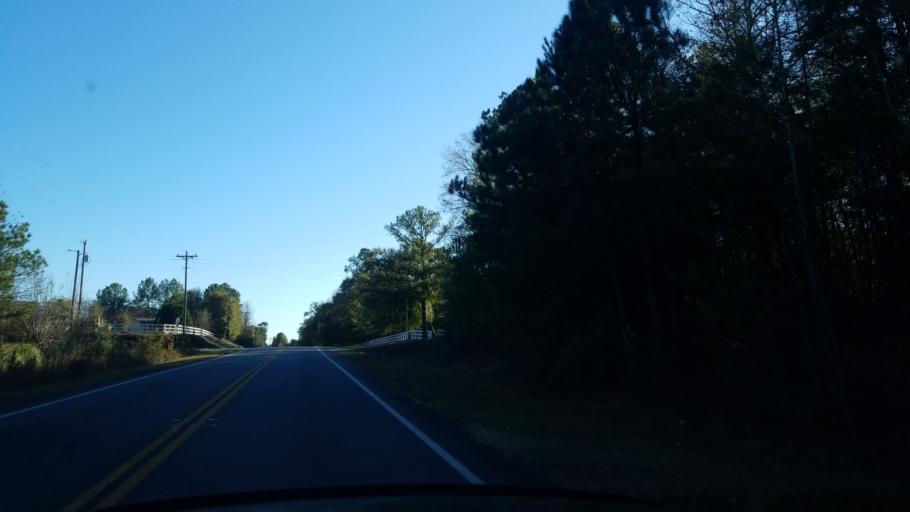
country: US
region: Georgia
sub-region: Talbot County
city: Talbotton
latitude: 32.5599
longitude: -84.6045
